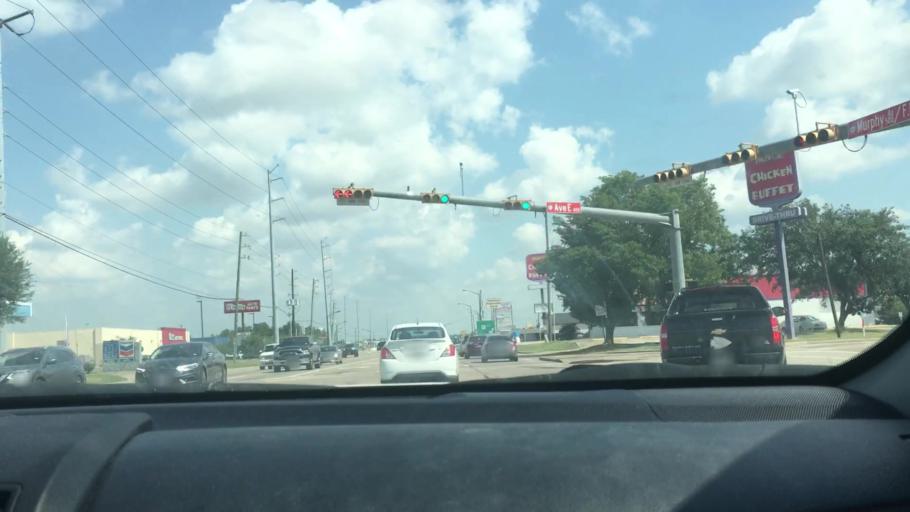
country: US
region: Texas
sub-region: Fort Bend County
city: Stafford
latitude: 29.6132
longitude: -95.5645
